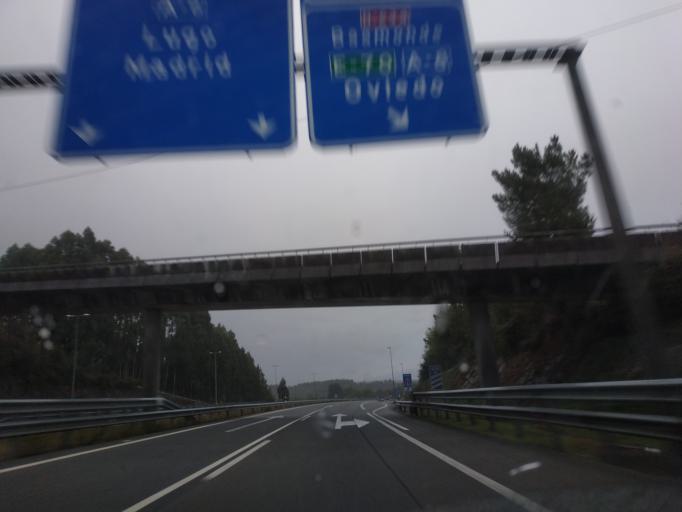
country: ES
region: Galicia
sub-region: Provincia de Lugo
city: Begonte
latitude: 43.1786
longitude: -7.7590
